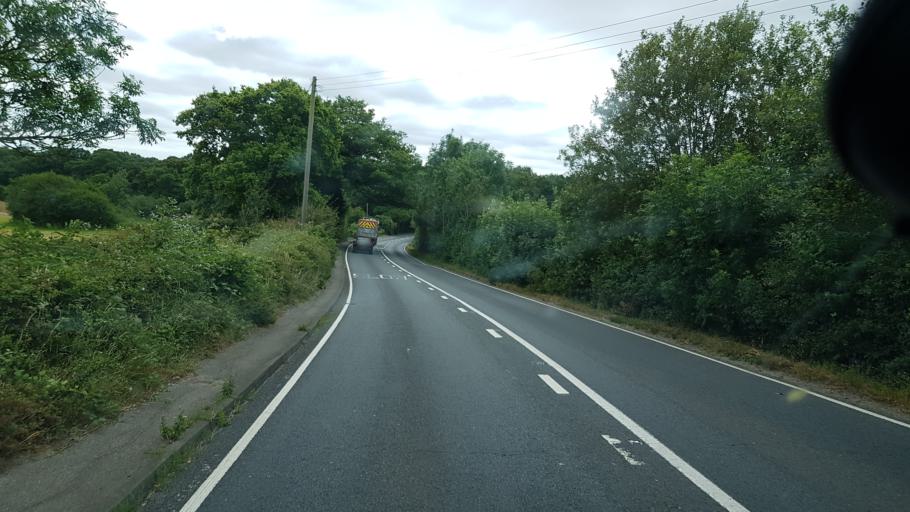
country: GB
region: England
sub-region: Surrey
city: Godstone
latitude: 51.2298
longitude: -0.0481
